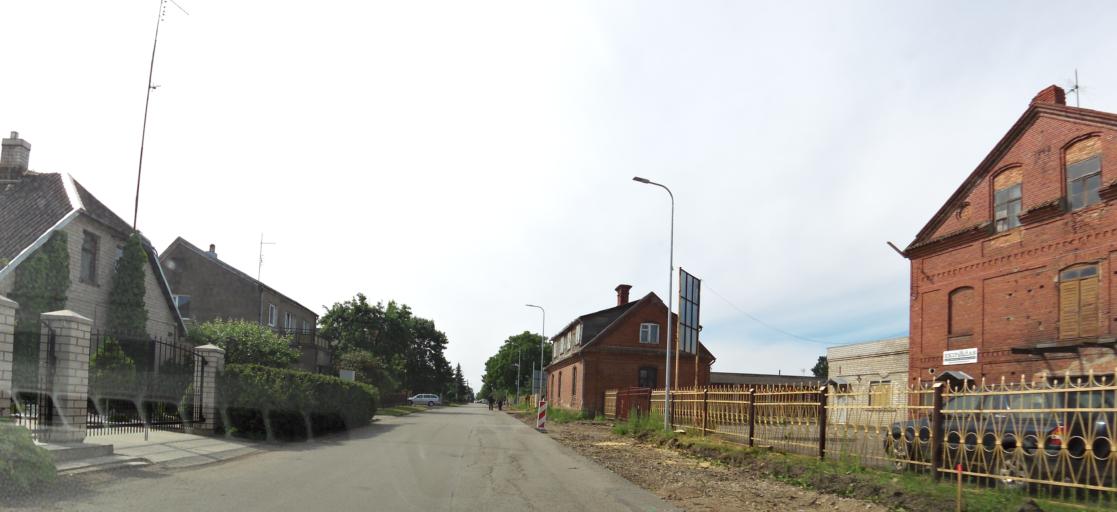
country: LT
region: Panevezys
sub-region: Birzai
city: Birzai
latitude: 56.2073
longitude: 24.7671
